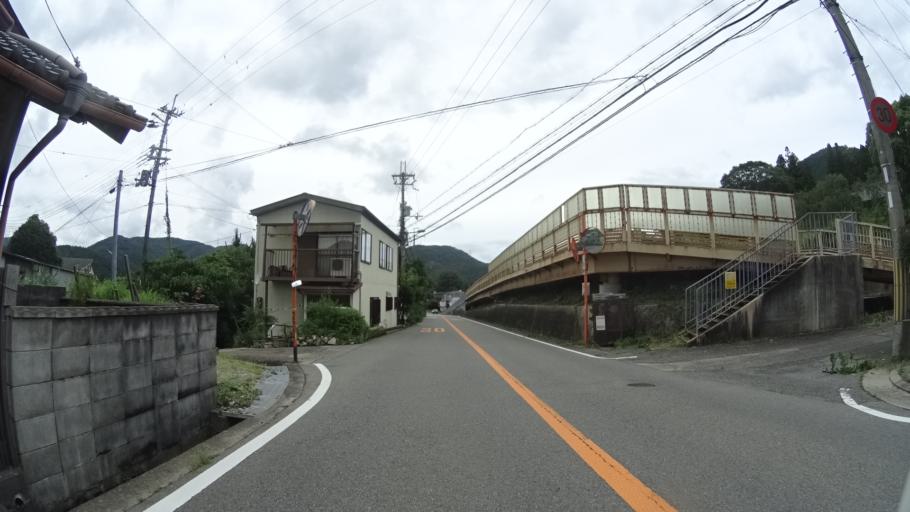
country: JP
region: Kyoto
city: Kameoka
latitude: 34.9716
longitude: 135.4654
